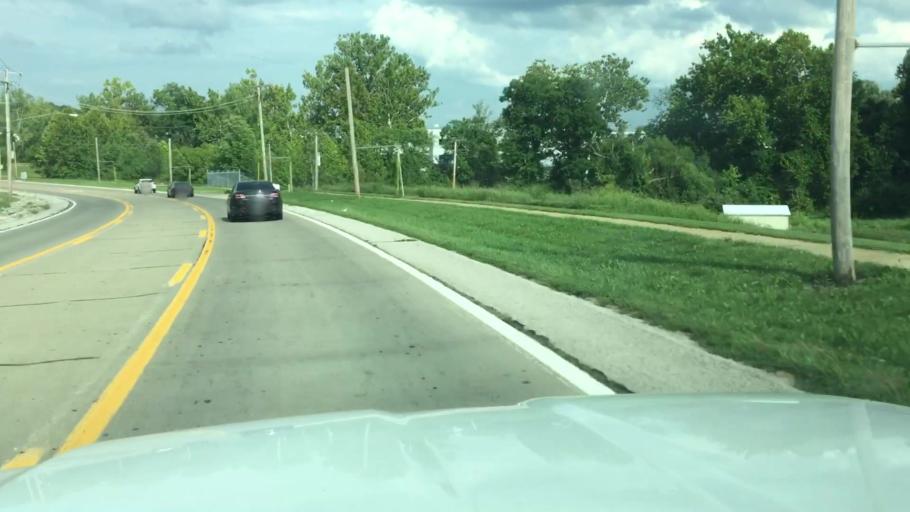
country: US
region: Missouri
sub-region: Jefferson County
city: Arnold
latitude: 38.4630
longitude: -90.3639
